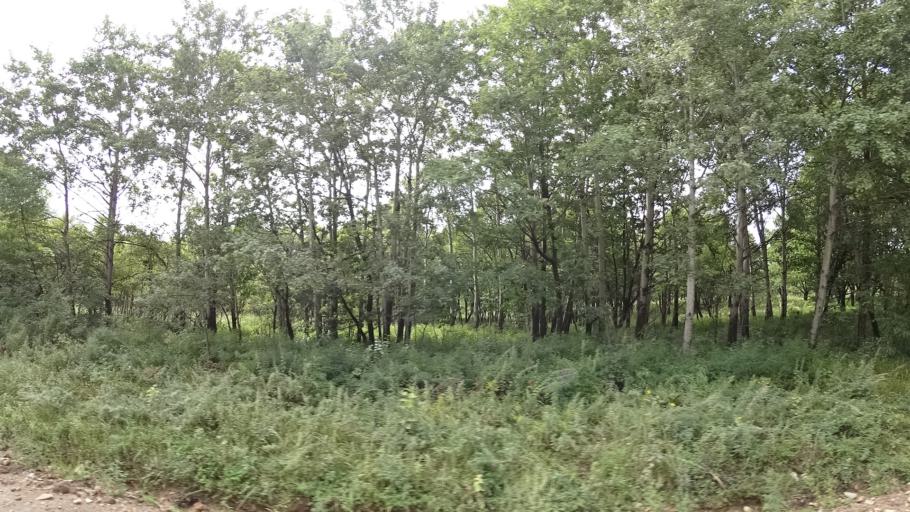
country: RU
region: Primorskiy
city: Lyalichi
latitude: 44.0915
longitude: 132.4339
